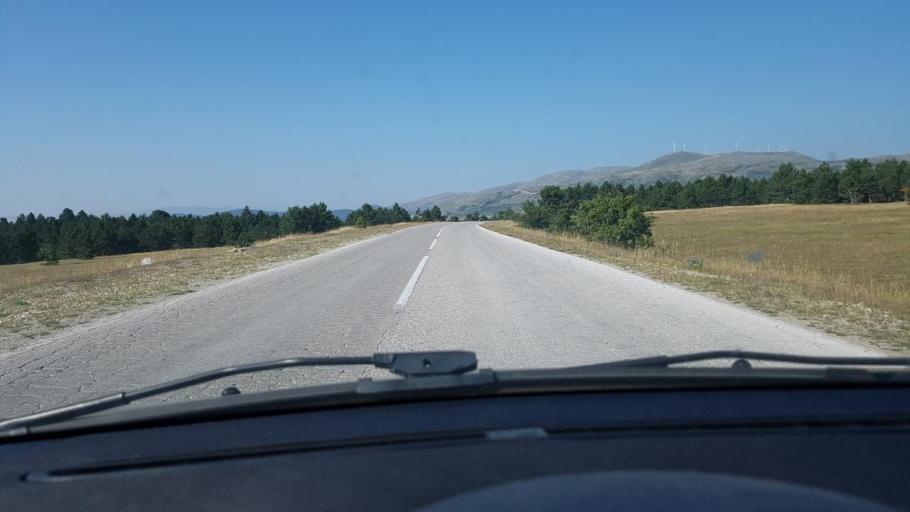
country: BA
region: Federation of Bosnia and Herzegovina
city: Tomislavgrad
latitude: 43.7887
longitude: 17.2365
